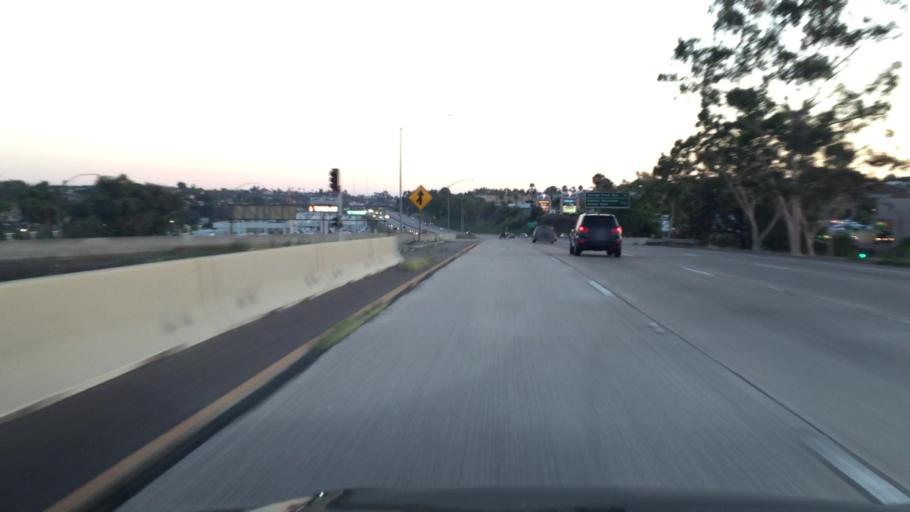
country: US
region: California
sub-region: San Diego County
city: Lemon Grove
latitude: 32.7428
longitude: -117.0498
